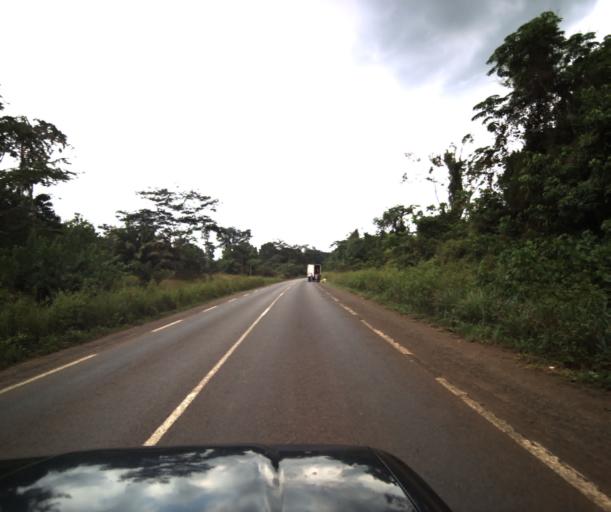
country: CM
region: Centre
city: Eseka
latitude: 3.8888
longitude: 10.7519
